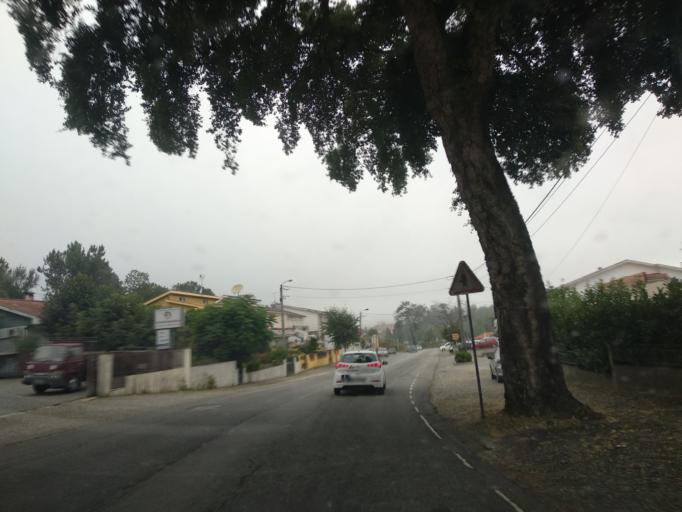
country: PT
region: Braga
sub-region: Vila Verde
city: Vila Verde
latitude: 41.6363
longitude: -8.4336
